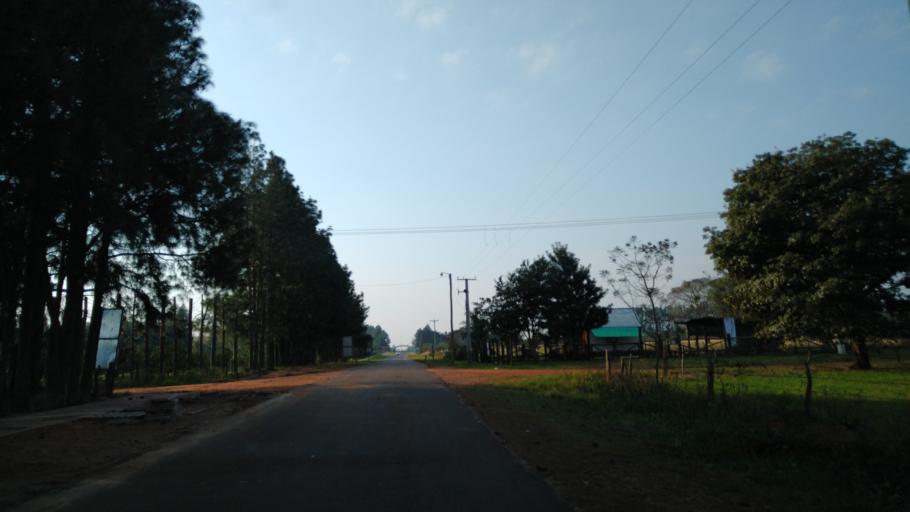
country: AR
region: Entre Rios
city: Santa Ana
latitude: -30.9049
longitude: -57.9252
